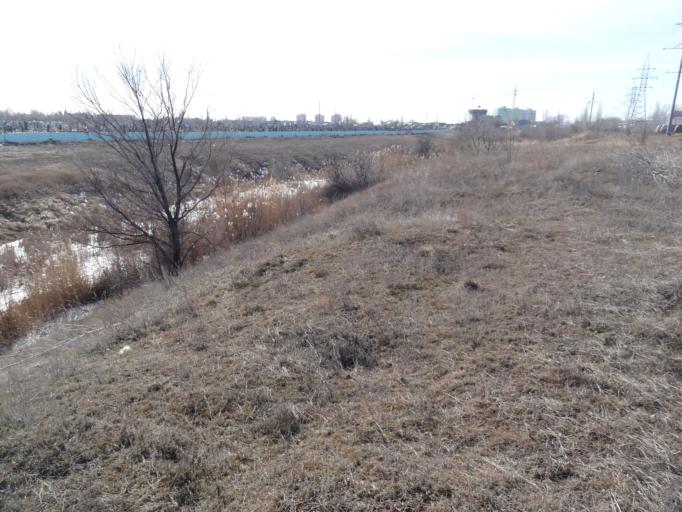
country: RU
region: Saratov
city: Shumeyka
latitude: 51.5081
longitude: 46.1924
